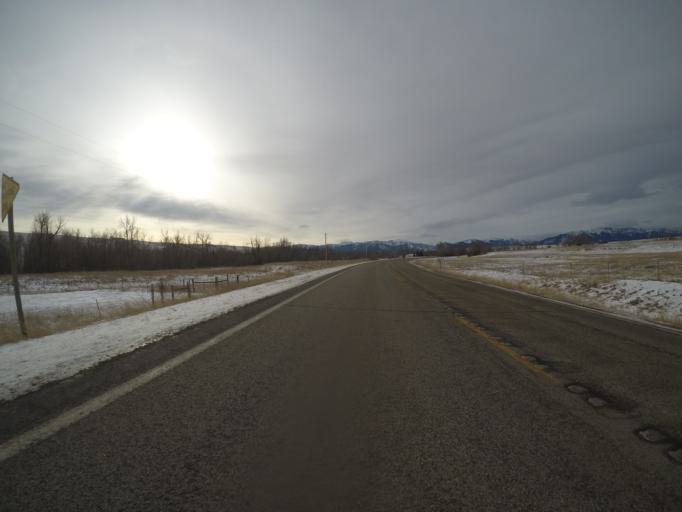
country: US
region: Montana
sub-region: Stillwater County
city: Absarokee
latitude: 45.4174
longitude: -109.4732
